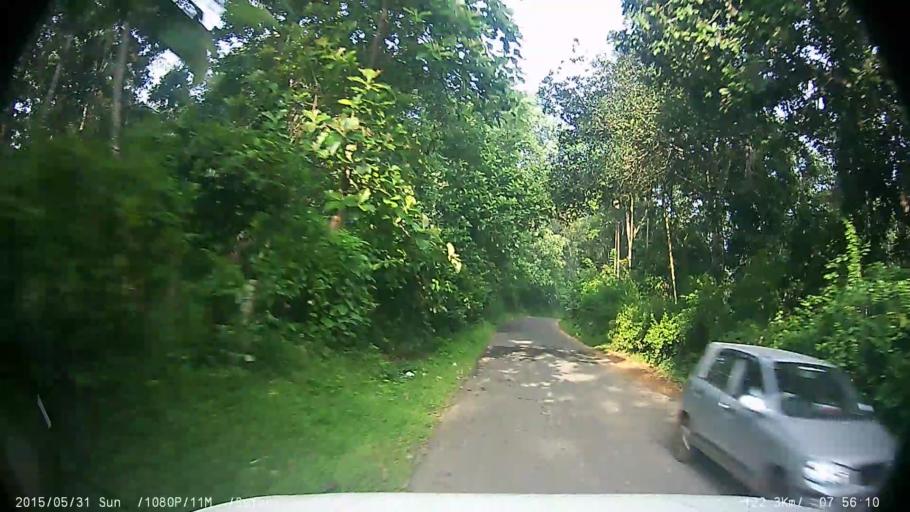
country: IN
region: Kerala
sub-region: Wayanad
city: Kalpetta
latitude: 11.6326
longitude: 76.0710
